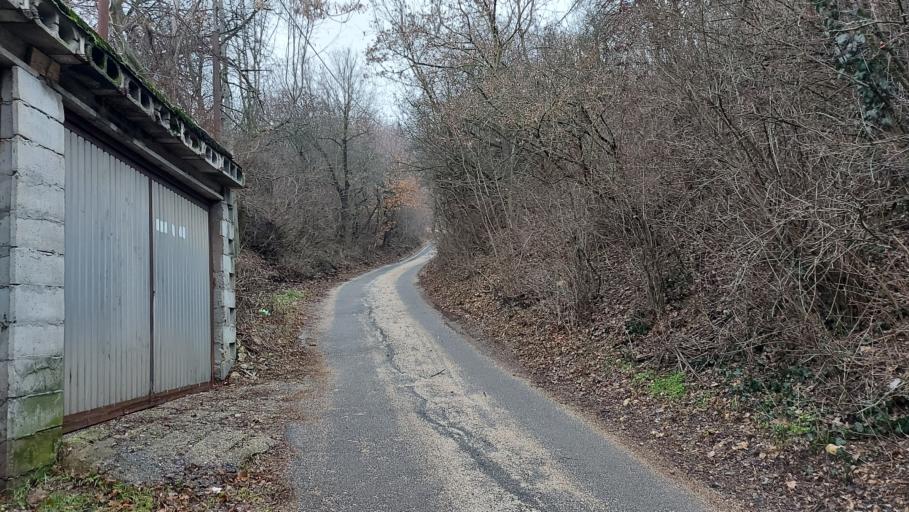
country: HU
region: Pest
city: Budaors
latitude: 47.4753
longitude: 18.9600
